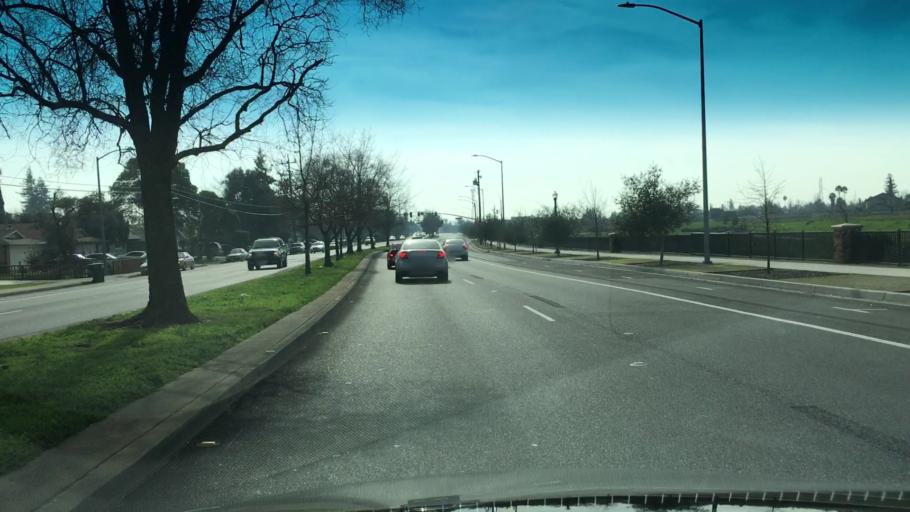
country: US
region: California
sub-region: Sacramento County
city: Parkway
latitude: 38.4803
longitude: -121.4525
